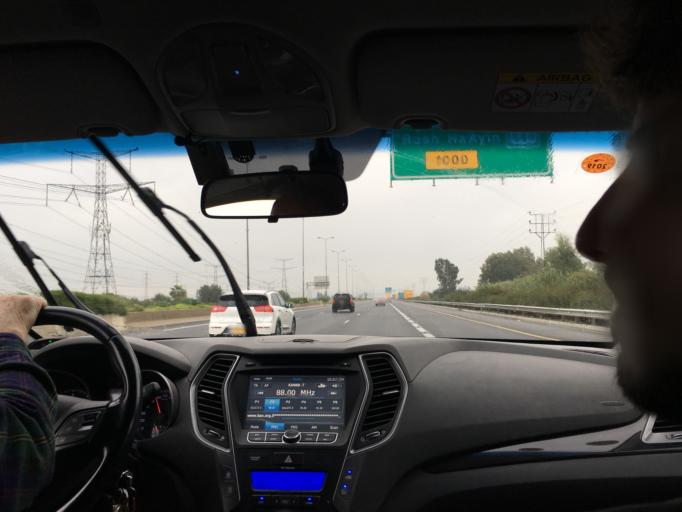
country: IL
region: Central District
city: Petah Tiqwa
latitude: 32.1194
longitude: 34.9144
